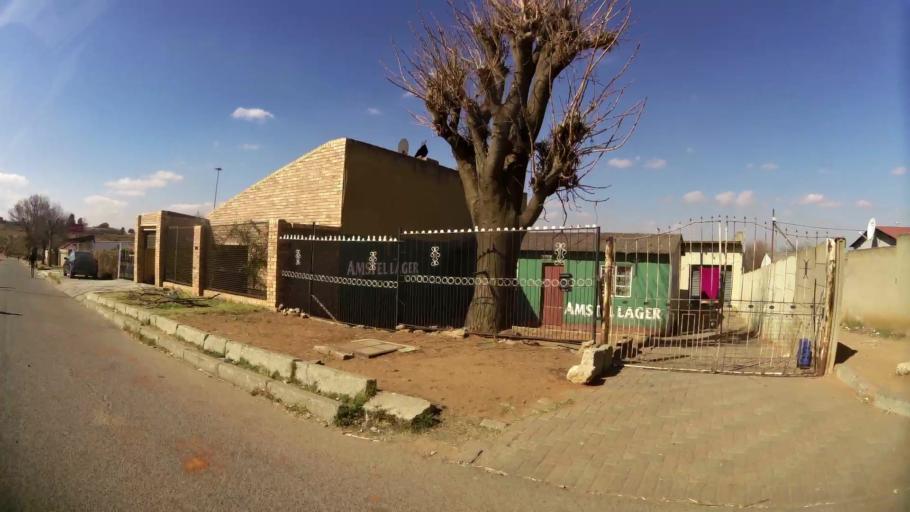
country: ZA
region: Gauteng
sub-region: City of Johannesburg Metropolitan Municipality
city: Soweto
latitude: -26.2236
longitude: 27.9107
